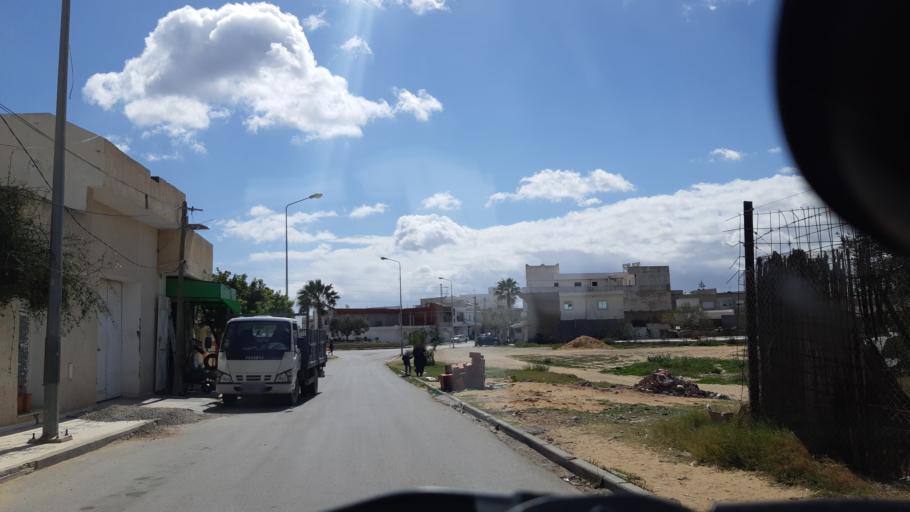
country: TN
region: Susah
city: Akouda
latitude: 35.8856
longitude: 10.5359
